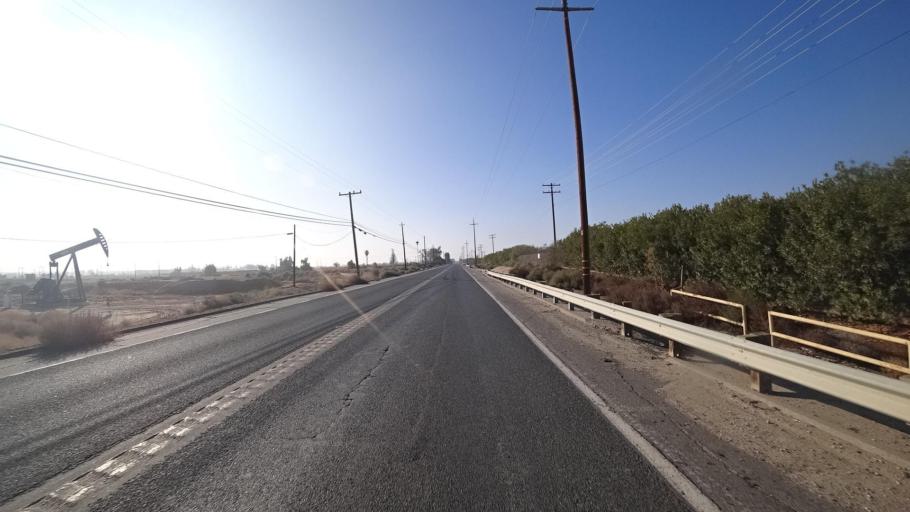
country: US
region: California
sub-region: Kern County
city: Oildale
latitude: 35.4269
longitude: -118.9976
